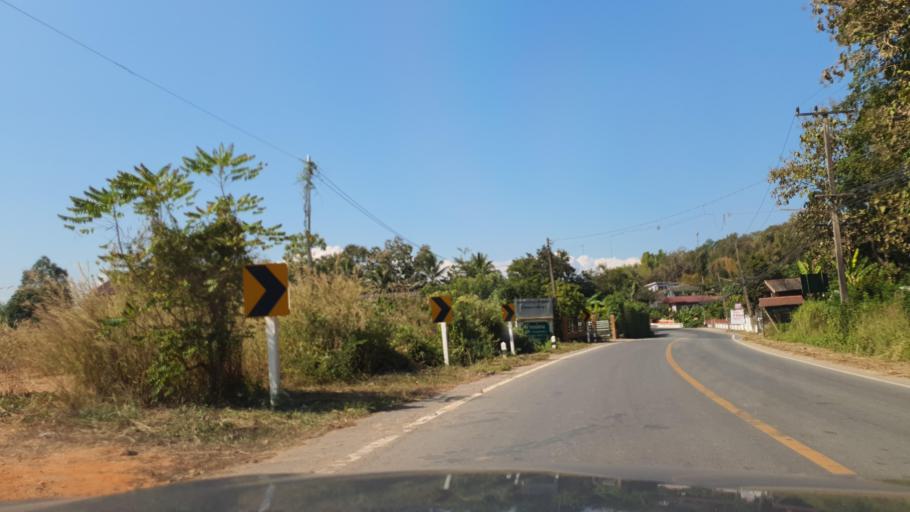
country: TH
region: Nan
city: Tha Wang Pha
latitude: 19.0811
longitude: 100.8849
